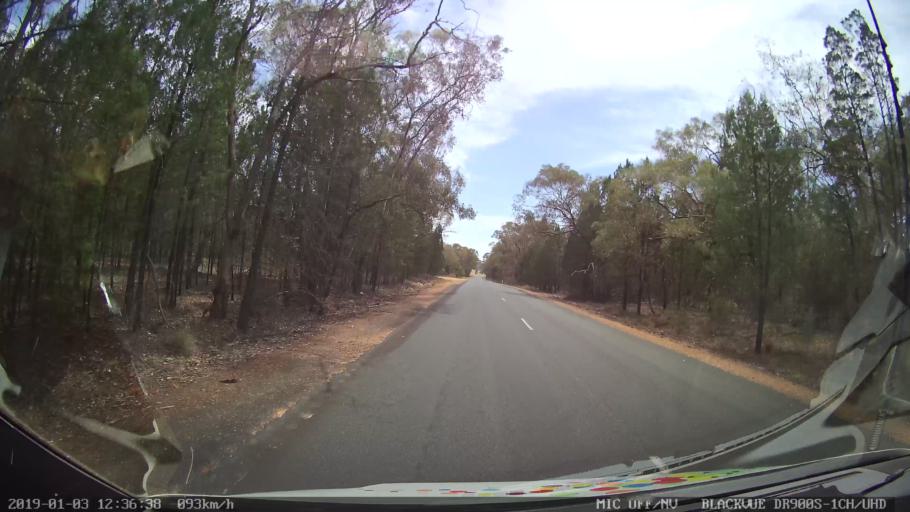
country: AU
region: New South Wales
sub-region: Weddin
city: Grenfell
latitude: -33.8523
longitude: 148.1779
